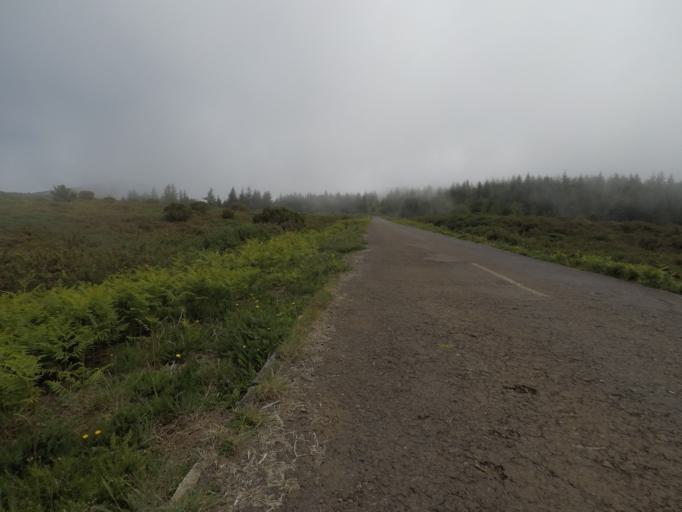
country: PT
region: Madeira
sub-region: Sao Vicente
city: Sao Vicente
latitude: 32.7691
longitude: -17.0790
